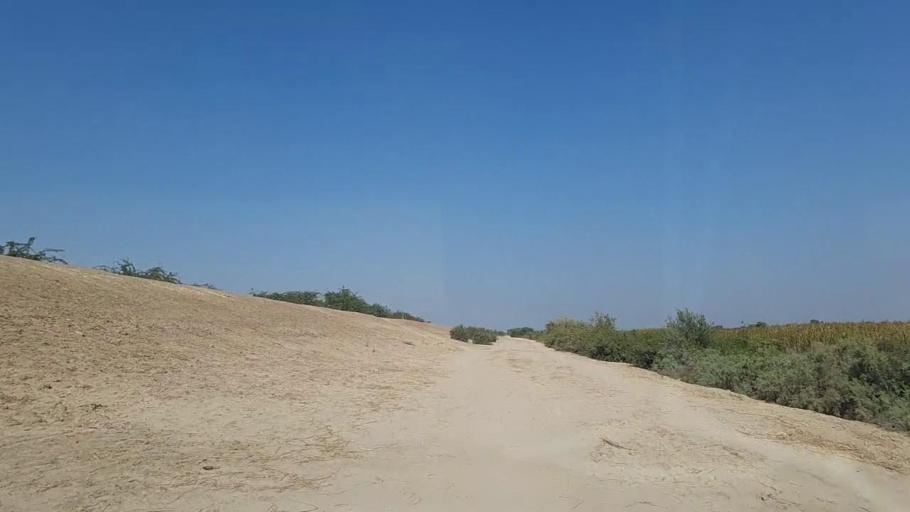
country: PK
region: Sindh
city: Chuhar Jamali
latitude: 24.4774
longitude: 68.0109
